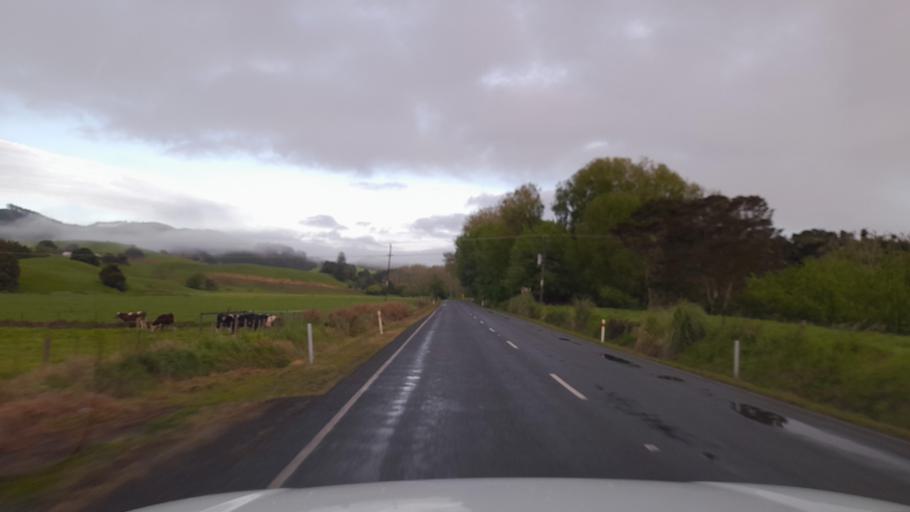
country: NZ
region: Northland
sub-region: Kaipara District
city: Dargaville
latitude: -35.7007
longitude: 173.9220
